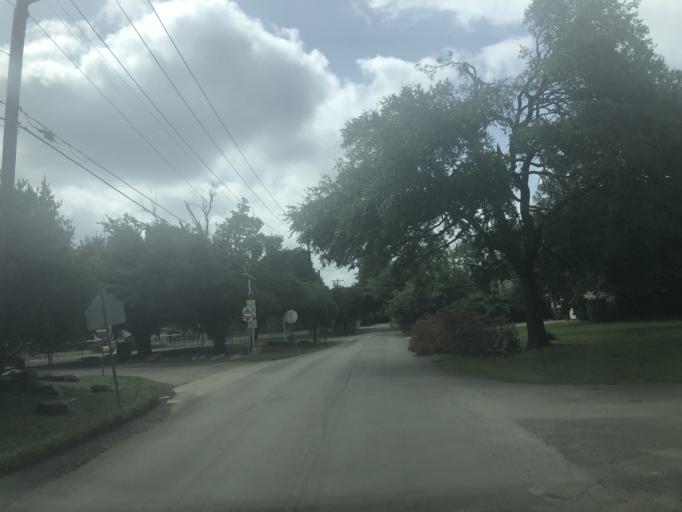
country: US
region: Texas
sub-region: Dallas County
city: University Park
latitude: 32.8552
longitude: -96.8330
